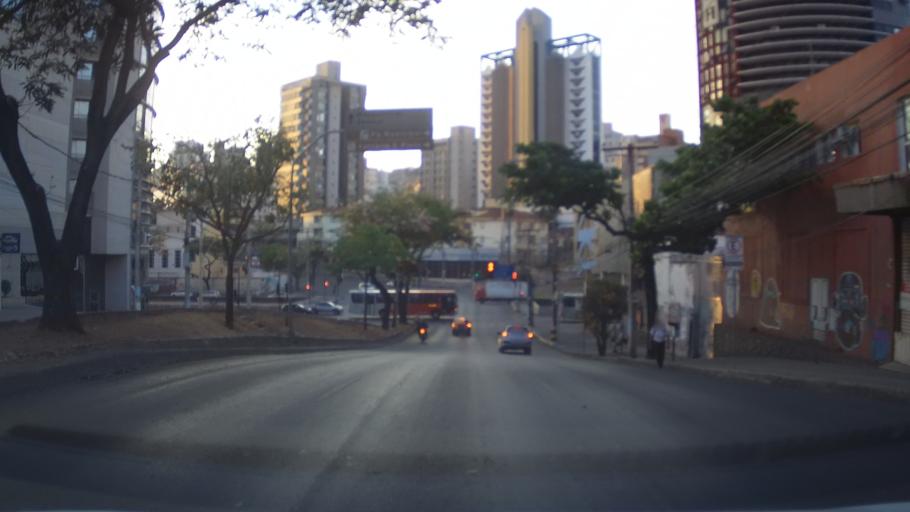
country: BR
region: Minas Gerais
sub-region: Belo Horizonte
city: Belo Horizonte
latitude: -19.9203
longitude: -43.9247
